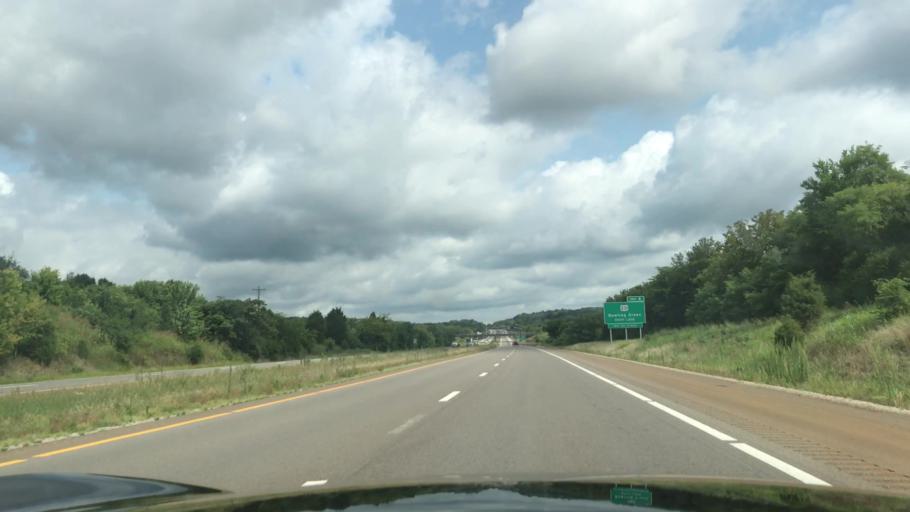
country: US
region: Kentucky
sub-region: Warren County
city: Bowling Green
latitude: 36.9854
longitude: -86.5023
